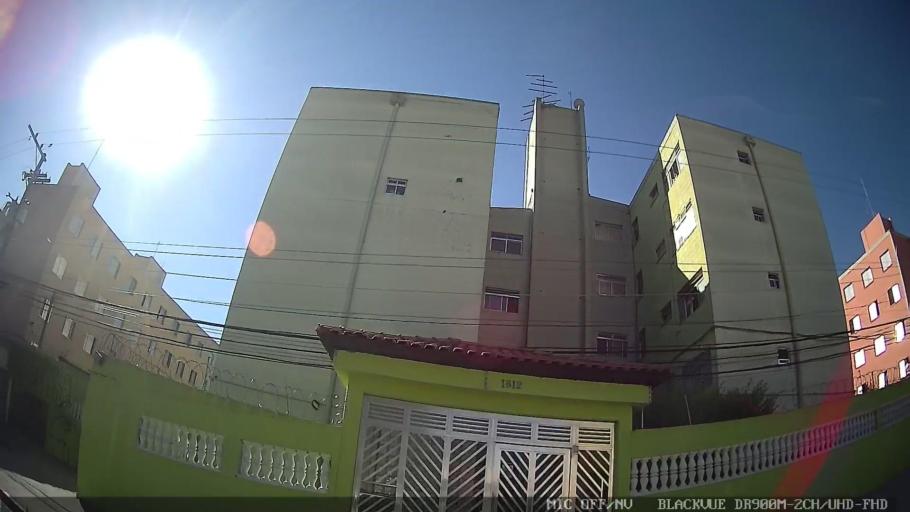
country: BR
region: Sao Paulo
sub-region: Sao Caetano Do Sul
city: Sao Caetano do Sul
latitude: -23.5514
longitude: -46.4825
